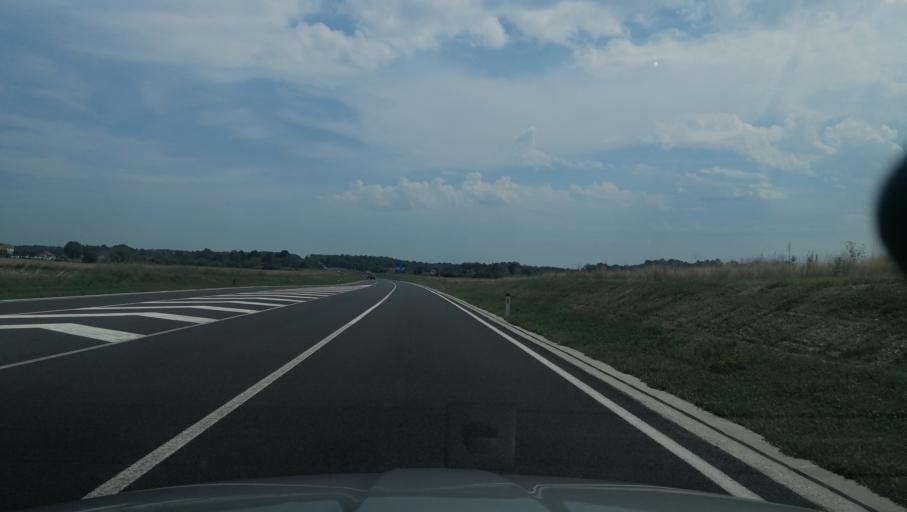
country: BA
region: Brcko
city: Brcko
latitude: 44.8377
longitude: 18.7788
